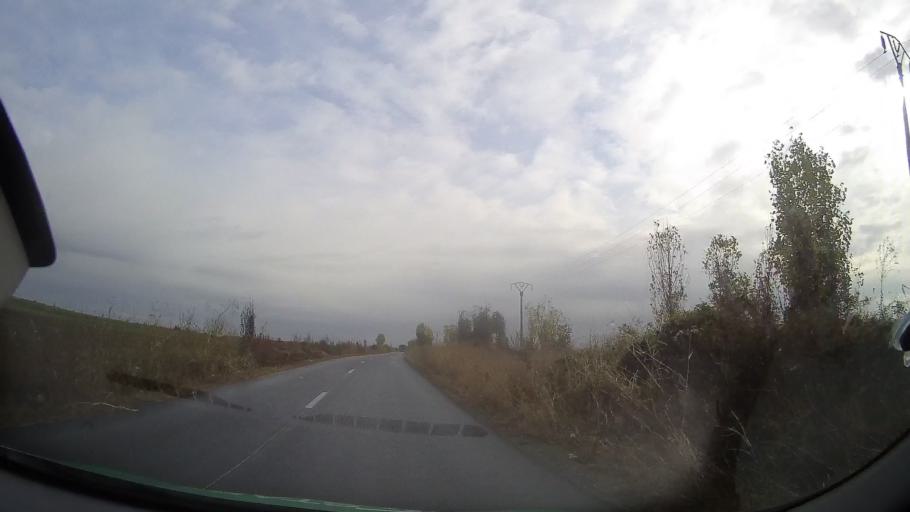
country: RO
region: Ialomita
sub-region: Comuna Maia
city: Maia
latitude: 44.7516
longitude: 26.3888
